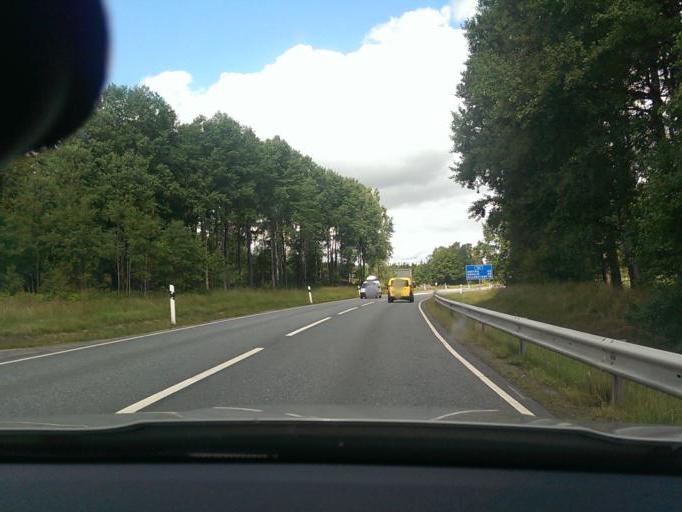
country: SE
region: Joenkoeping
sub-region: Varnamo Kommun
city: Varnamo
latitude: 57.2075
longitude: 14.0291
